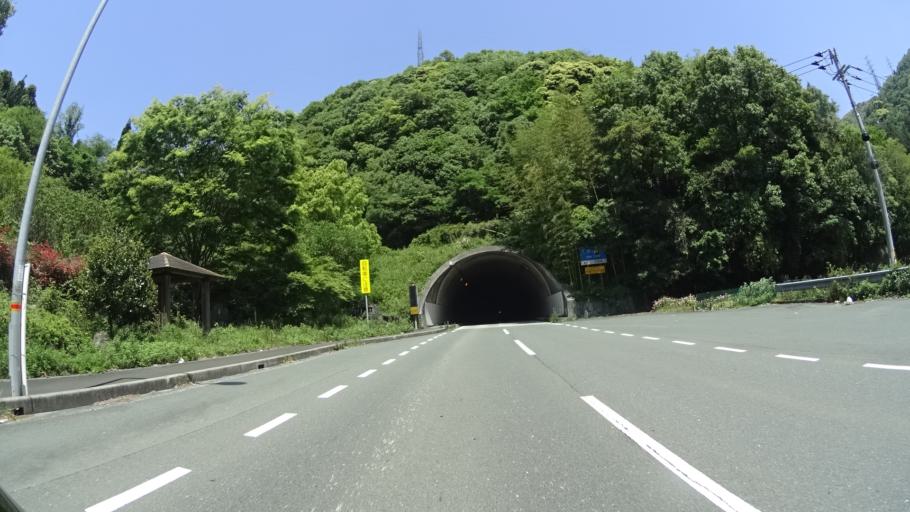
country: JP
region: Ehime
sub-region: Nishiuwa-gun
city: Ikata-cho
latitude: 33.5080
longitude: 132.3965
